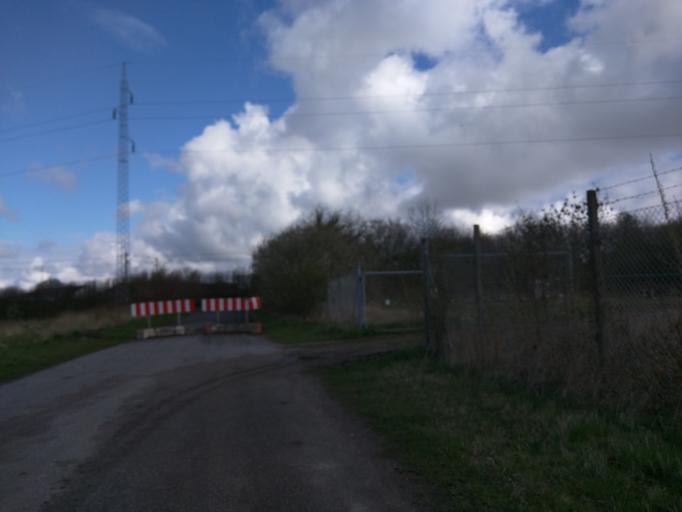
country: DK
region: South Denmark
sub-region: Fredericia Kommune
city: Snoghoj
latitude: 55.5412
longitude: 9.6921
